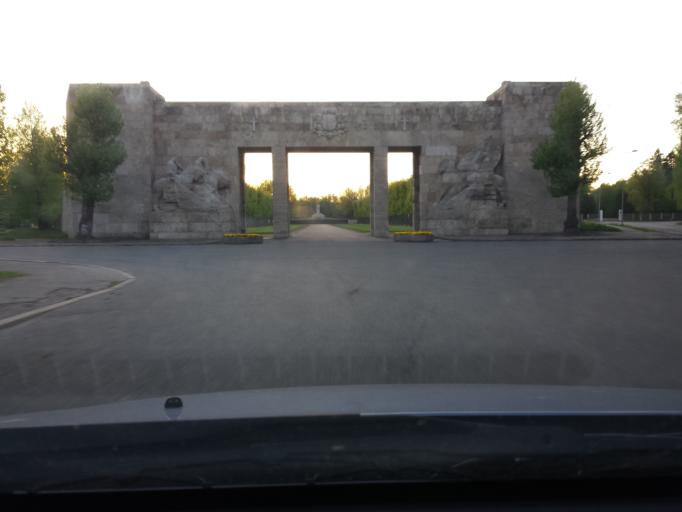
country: LV
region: Riga
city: Riga
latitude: 56.9853
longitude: 24.1476
